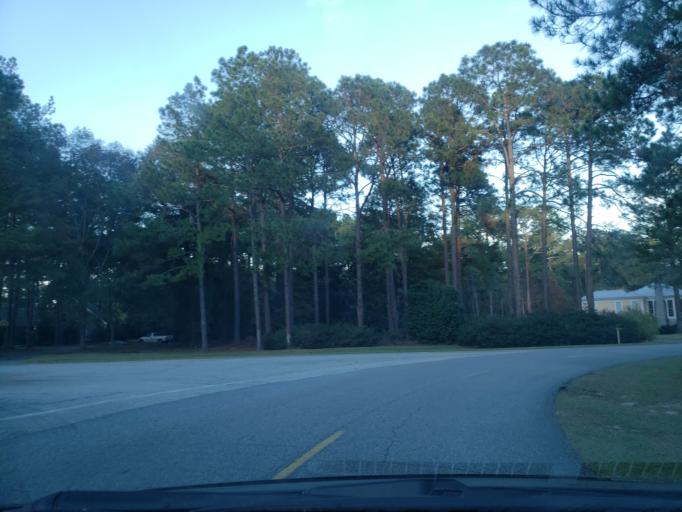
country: US
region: Georgia
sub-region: Tift County
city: Tifton
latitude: 31.4515
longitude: -83.5917
